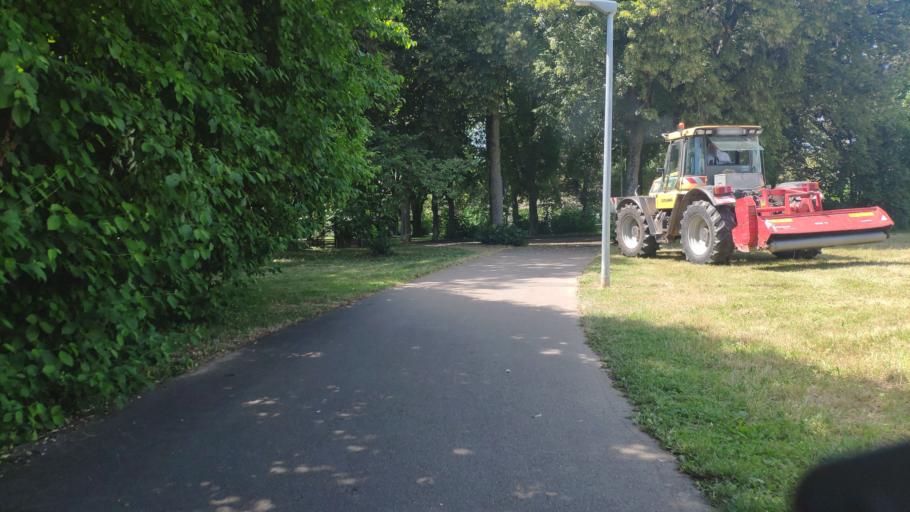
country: DE
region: Baden-Wuerttemberg
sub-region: Regierungsbezirk Stuttgart
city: Goeppingen
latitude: 48.6965
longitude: 9.6709
